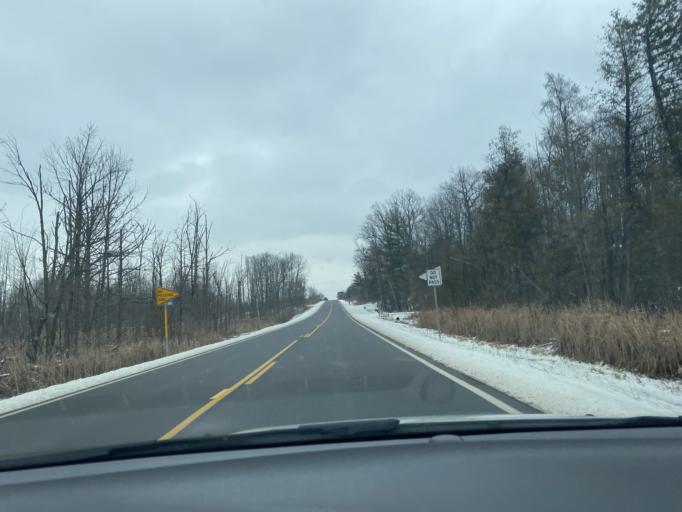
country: US
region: Michigan
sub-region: Lapeer County
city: North Branch
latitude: 43.2070
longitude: -83.2146
